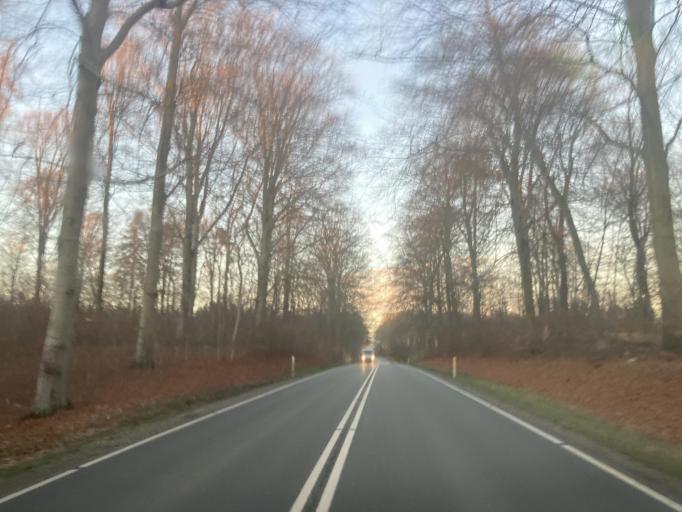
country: DK
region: Capital Region
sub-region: Gribskov Kommune
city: Graested
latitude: 56.0402
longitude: 12.2826
